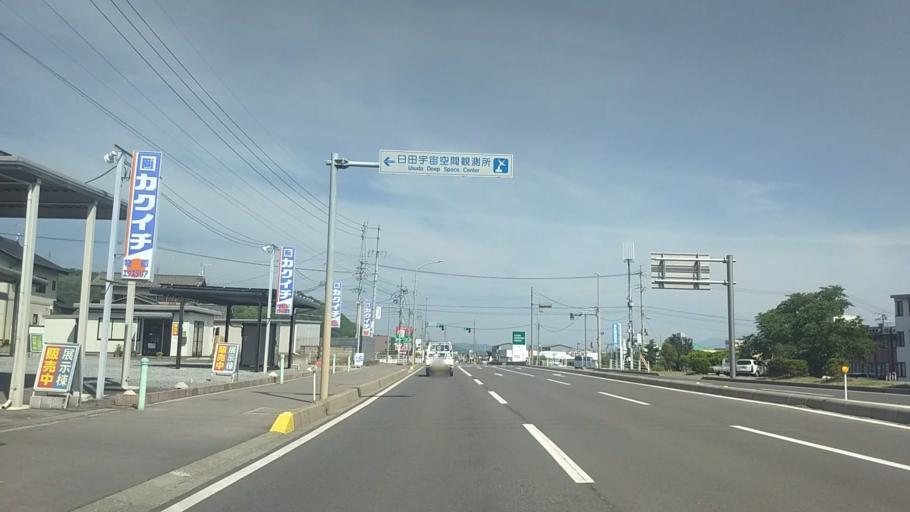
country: JP
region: Nagano
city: Saku
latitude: 36.1935
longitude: 138.4786
